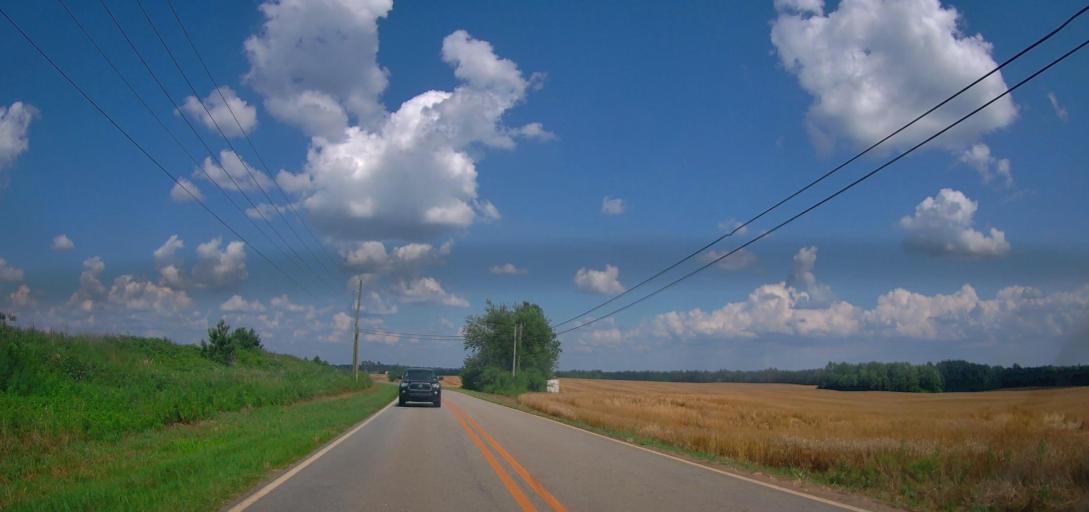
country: US
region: Georgia
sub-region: Spalding County
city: East Griffin
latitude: 33.2262
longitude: -84.1205
